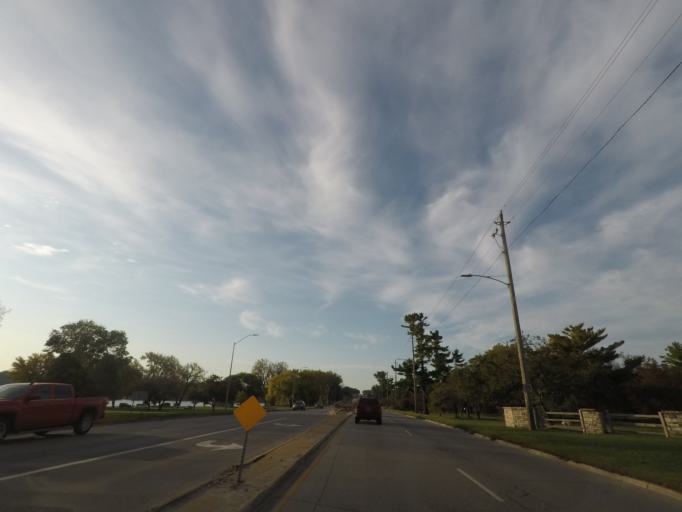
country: US
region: Iowa
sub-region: Polk County
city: Des Moines
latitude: 41.5735
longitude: -93.6450
